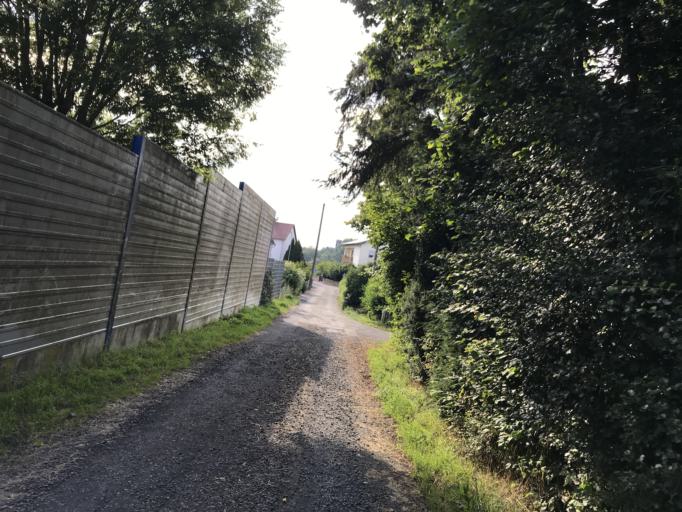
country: DE
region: Hesse
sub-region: Regierungsbezirk Giessen
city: Lich
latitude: 50.5143
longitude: 8.8295
